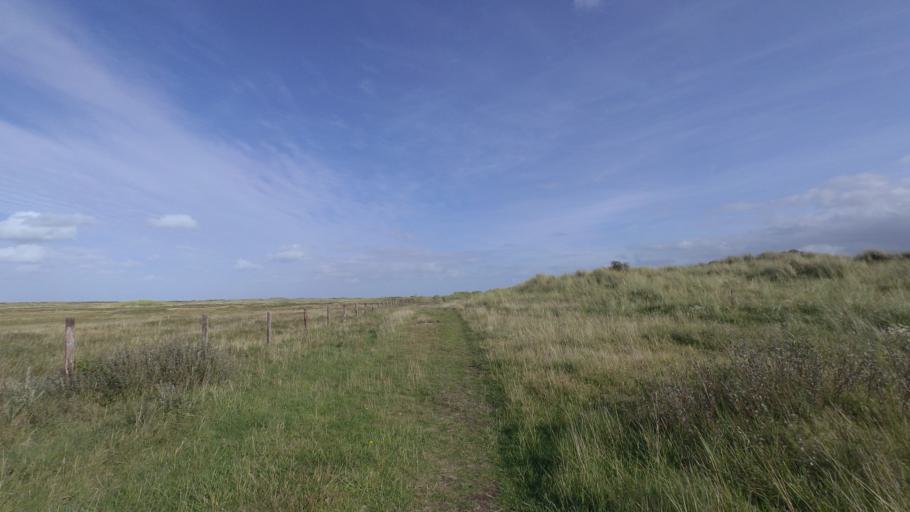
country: NL
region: Friesland
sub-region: Gemeente Ameland
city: Nes
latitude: 53.4527
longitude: 5.8472
